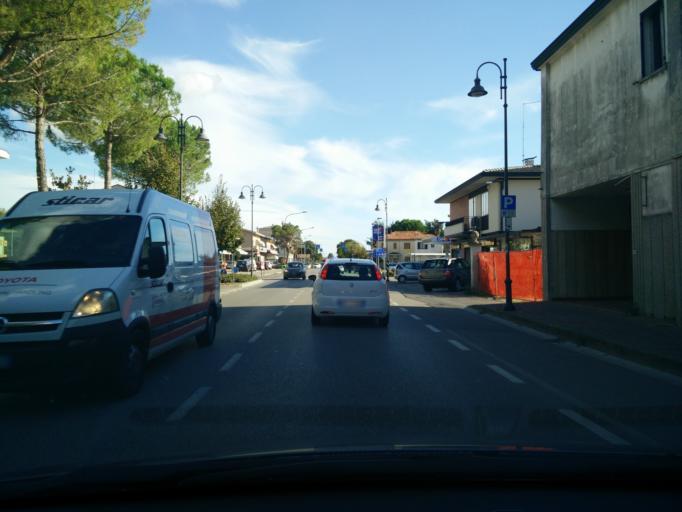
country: IT
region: Veneto
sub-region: Provincia di Venezia
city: Noventa di Piave
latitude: 45.6596
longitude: 12.5311
